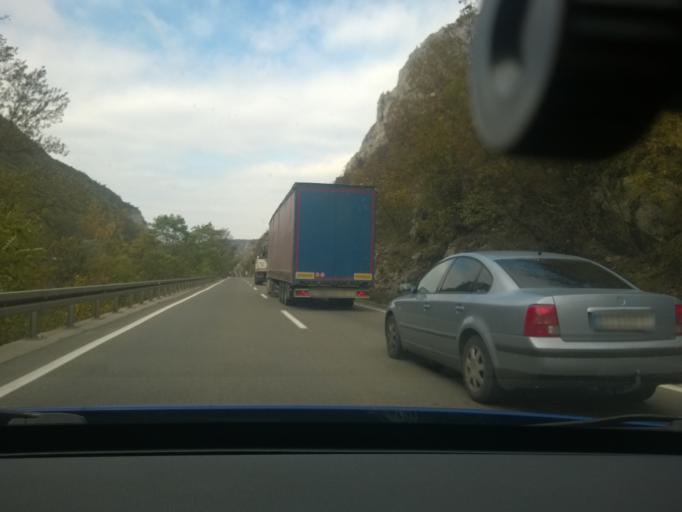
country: RS
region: Central Serbia
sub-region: Nisavski Okrug
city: Svrljig
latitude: 43.3327
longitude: 22.1482
